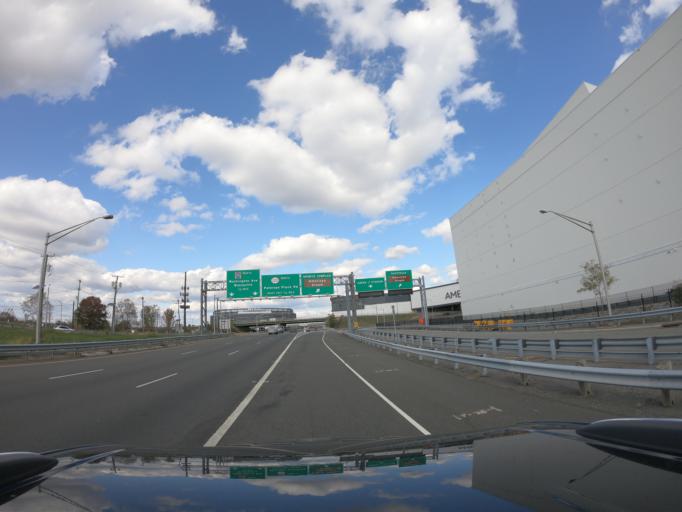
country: US
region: New Jersey
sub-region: Hudson County
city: Secaucus
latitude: 40.8062
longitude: -74.0724
